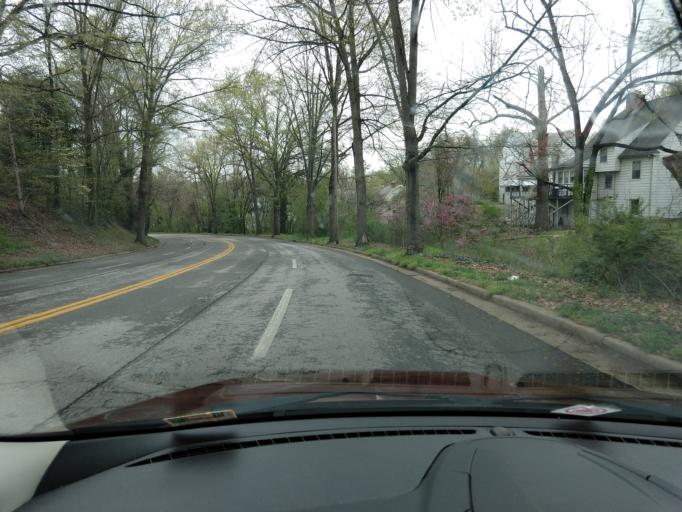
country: US
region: Virginia
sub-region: City of Danville
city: Danville
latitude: 36.5729
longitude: -79.4312
